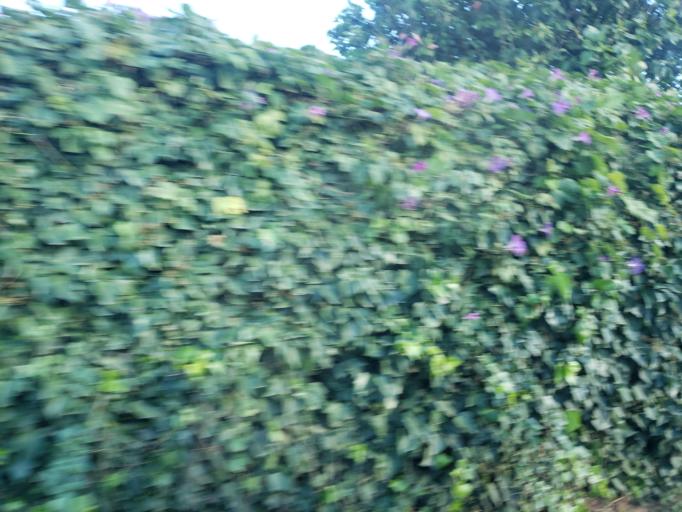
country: PT
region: Faro
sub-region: Portimao
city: Alvor
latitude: 37.1934
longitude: -8.5894
